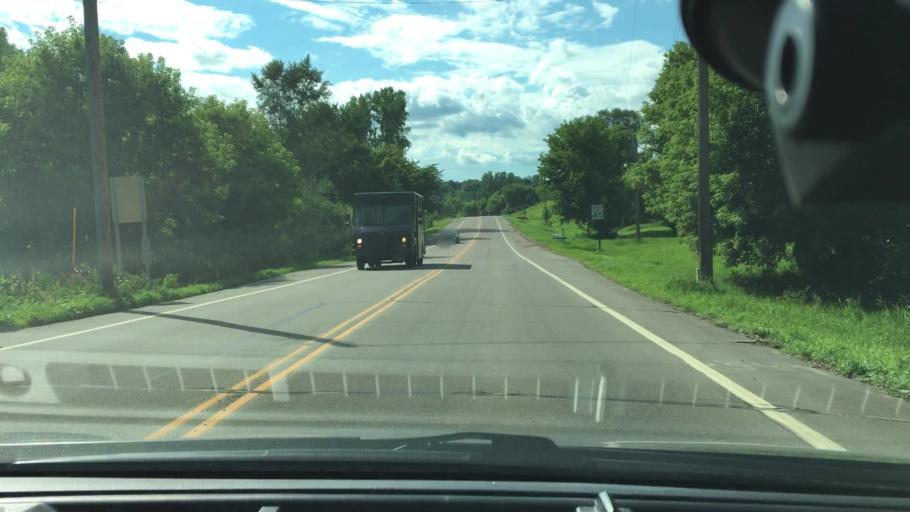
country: US
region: Minnesota
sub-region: Hennepin County
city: Minnetrista
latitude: 44.9226
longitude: -93.6989
